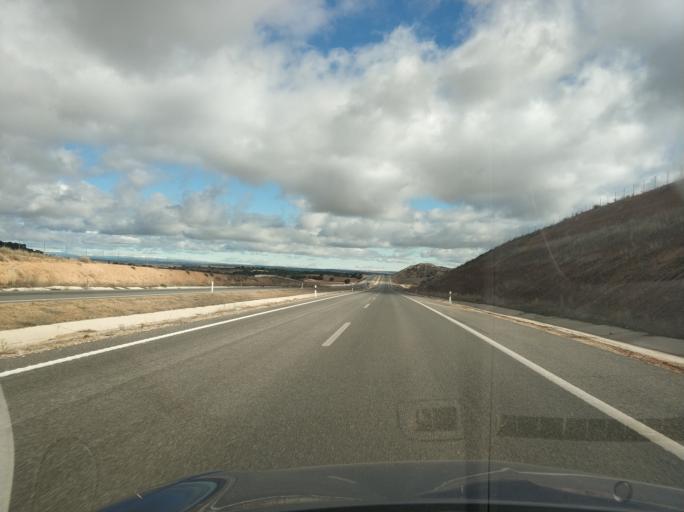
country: ES
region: Castille and Leon
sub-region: Provincia de Burgos
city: Campillo de Aranda
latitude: 41.6331
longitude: -3.7443
